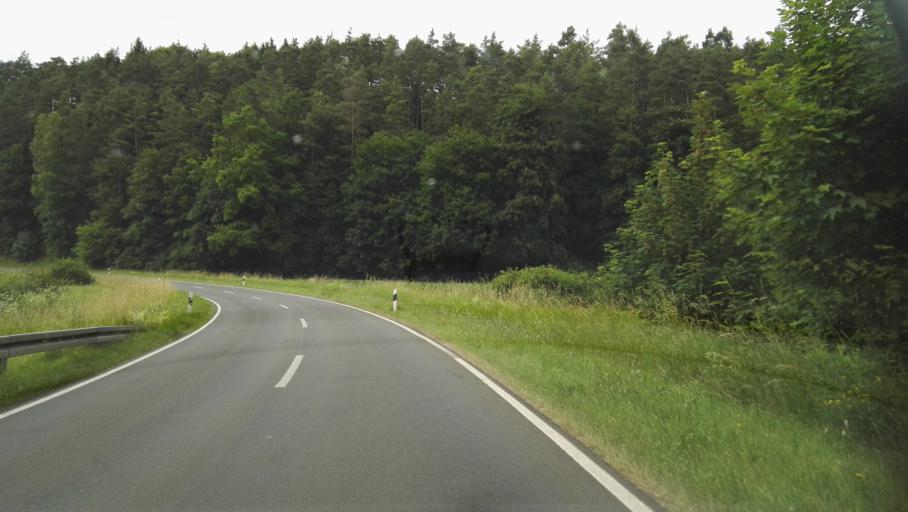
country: DE
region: Bavaria
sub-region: Upper Franconia
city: Plankenfels
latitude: 49.8762
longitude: 11.3432
